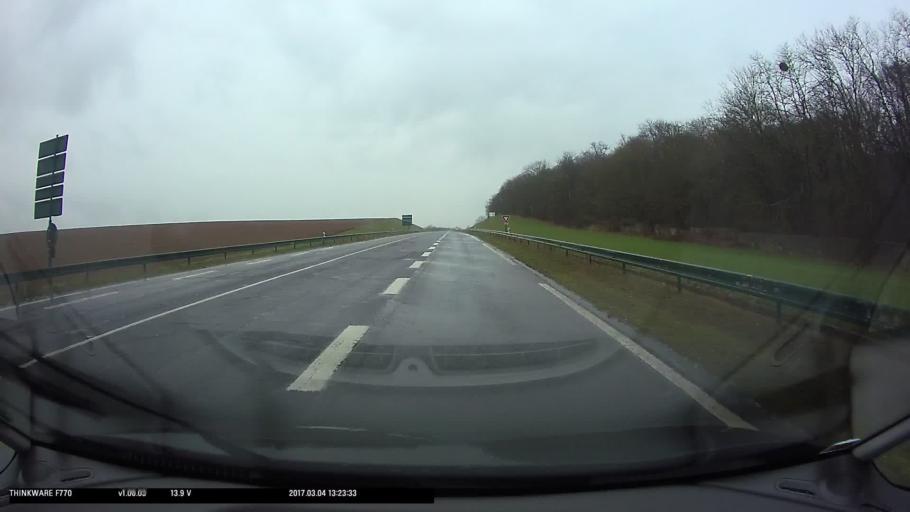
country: FR
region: Ile-de-France
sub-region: Departement du Val-d'Oise
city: Marines
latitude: 49.1333
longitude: 1.9793
